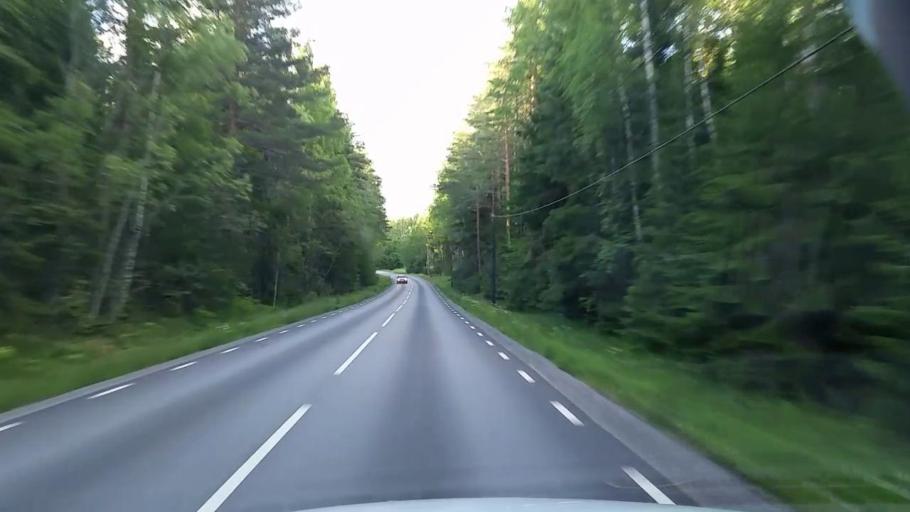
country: SE
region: Vaestmanland
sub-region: Kopings Kommun
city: Kolsva
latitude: 59.6445
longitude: 15.8275
